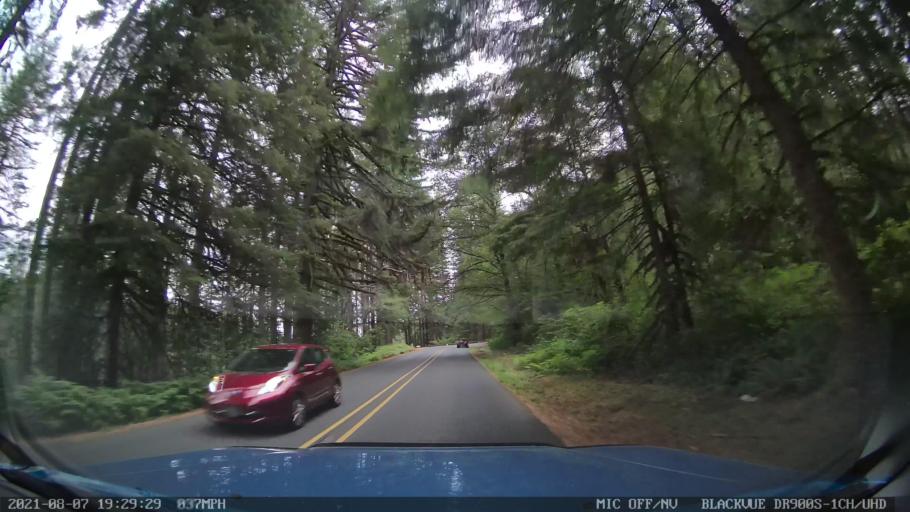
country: US
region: Oregon
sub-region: Linn County
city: Lyons
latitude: 44.8837
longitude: -122.6284
